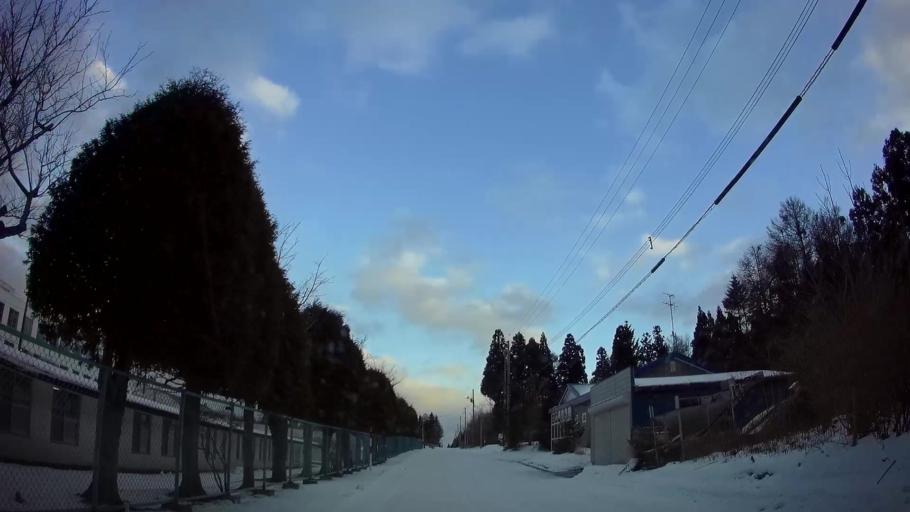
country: JP
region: Hokkaido
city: Nanae
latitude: 42.0227
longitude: 140.8333
